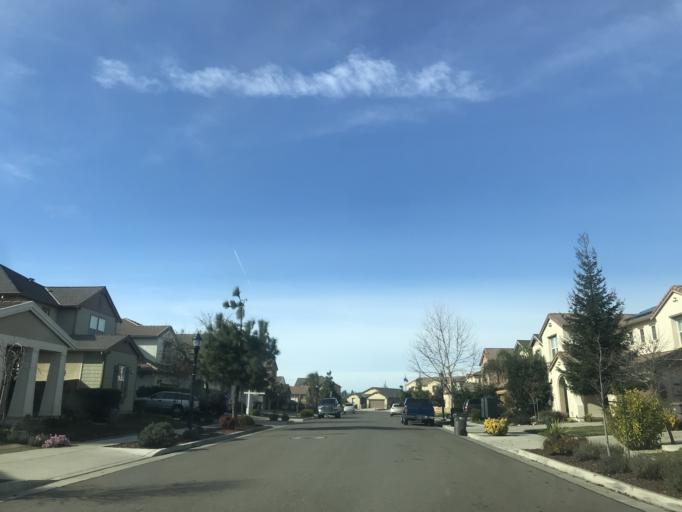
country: US
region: California
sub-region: Yolo County
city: Woodland
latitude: 38.6588
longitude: -121.7590
